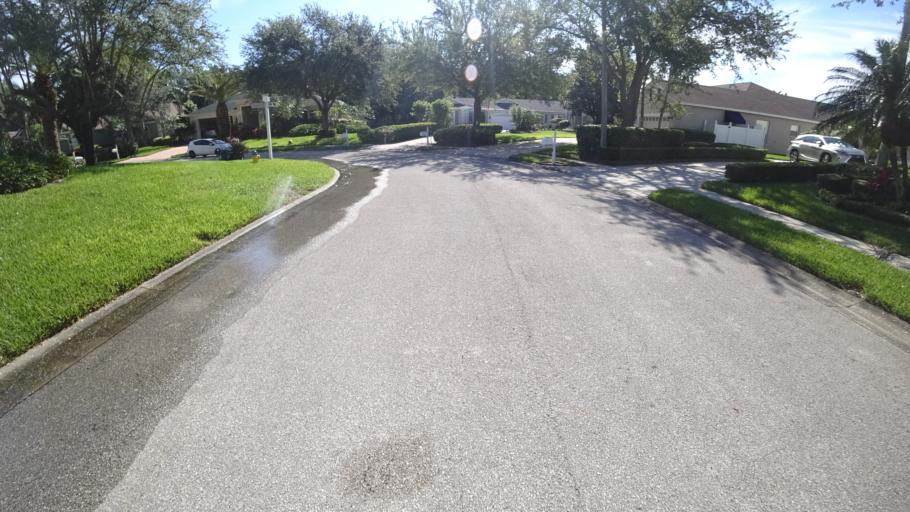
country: US
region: Florida
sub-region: Manatee County
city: West Bradenton
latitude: 27.5089
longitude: -82.6555
